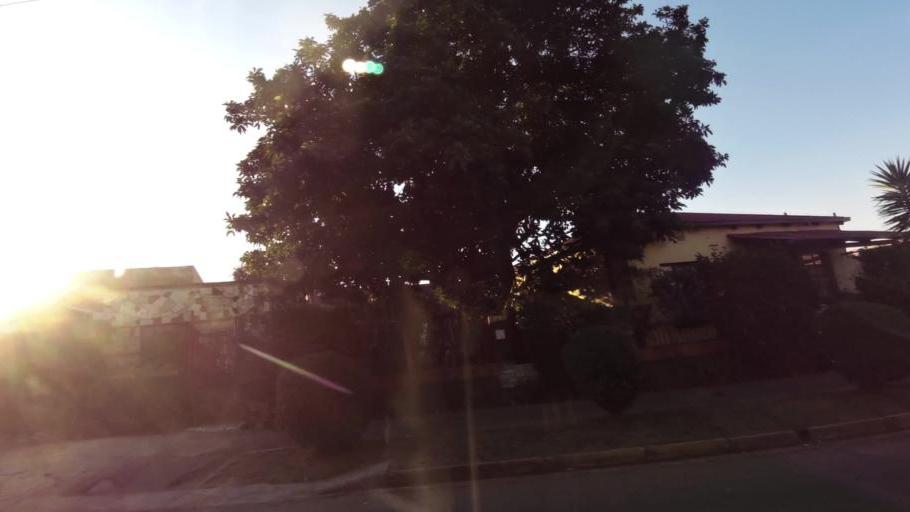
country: ZA
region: Gauteng
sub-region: City of Johannesburg Metropolitan Municipality
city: Roodepoort
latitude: -26.1734
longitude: 27.9567
